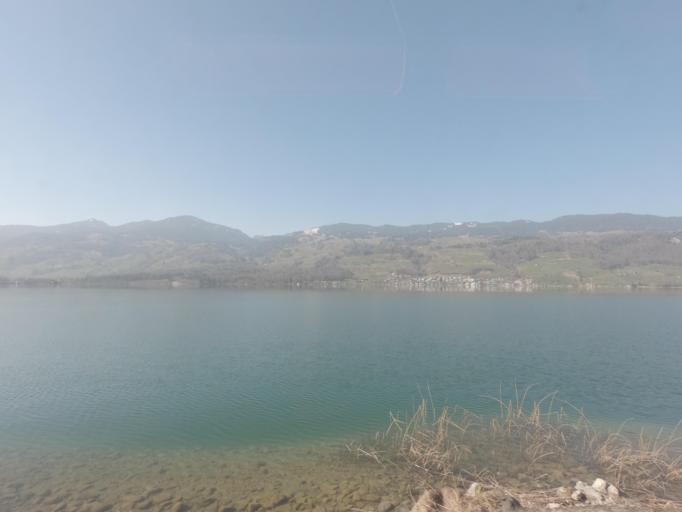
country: CH
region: Obwalden
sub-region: Obwalden
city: Sachseln
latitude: 46.8519
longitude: 8.2110
